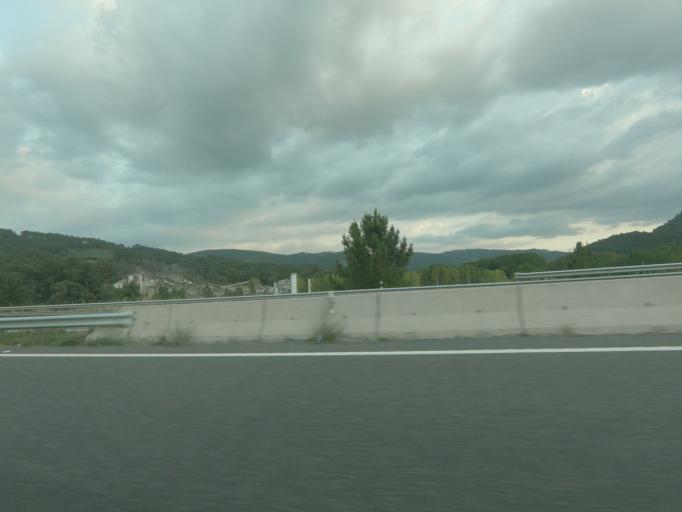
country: ES
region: Galicia
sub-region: Provincia de Ourense
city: Punxin
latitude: 42.3428
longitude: -8.0034
